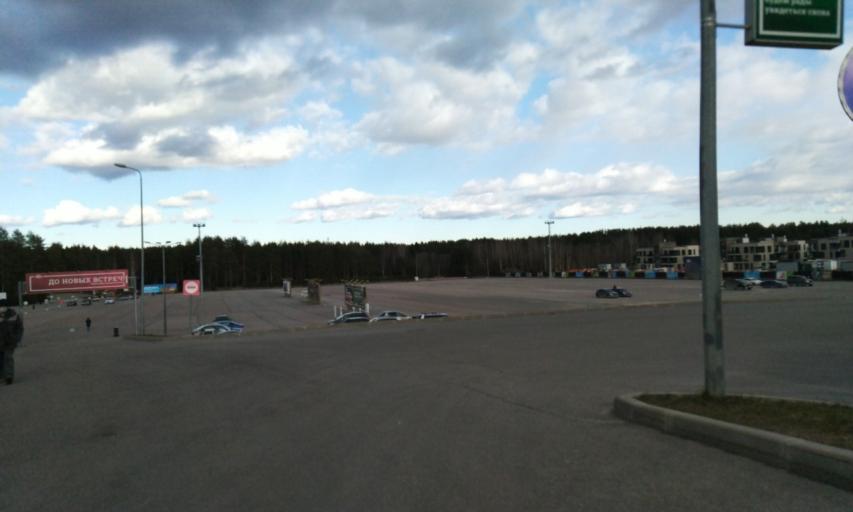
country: RU
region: Leningrad
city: Novoye Devyatkino
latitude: 60.1262
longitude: 30.4430
